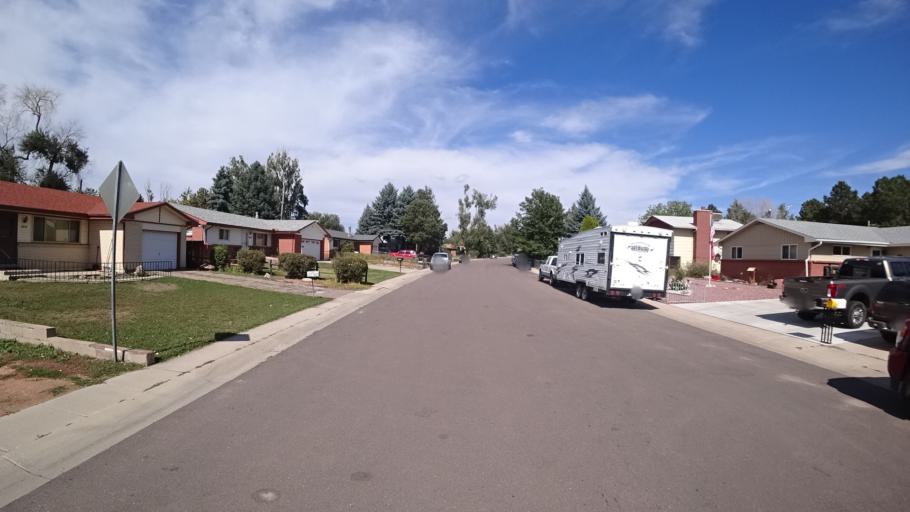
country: US
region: Colorado
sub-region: El Paso County
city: Cimarron Hills
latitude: 38.8926
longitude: -104.7634
